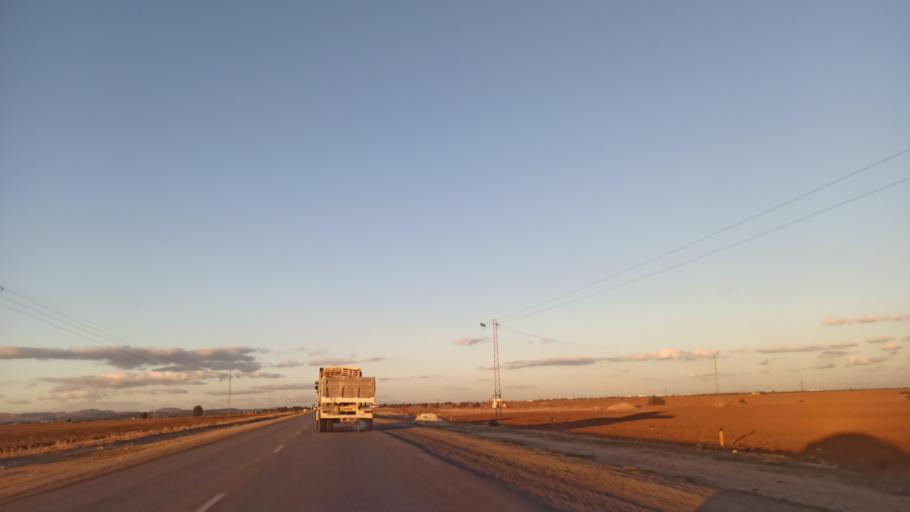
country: TN
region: Susah
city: Harqalah
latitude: 36.0847
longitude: 10.3538
